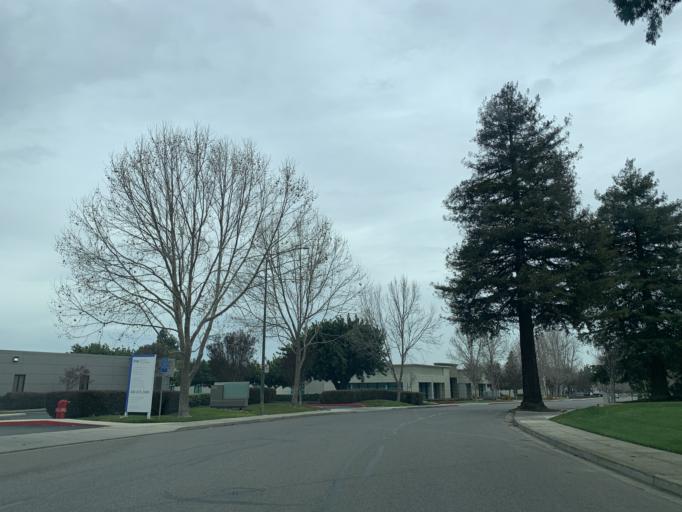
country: US
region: California
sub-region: Santa Clara County
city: Sunnyvale
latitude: 37.3879
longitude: -122.0516
